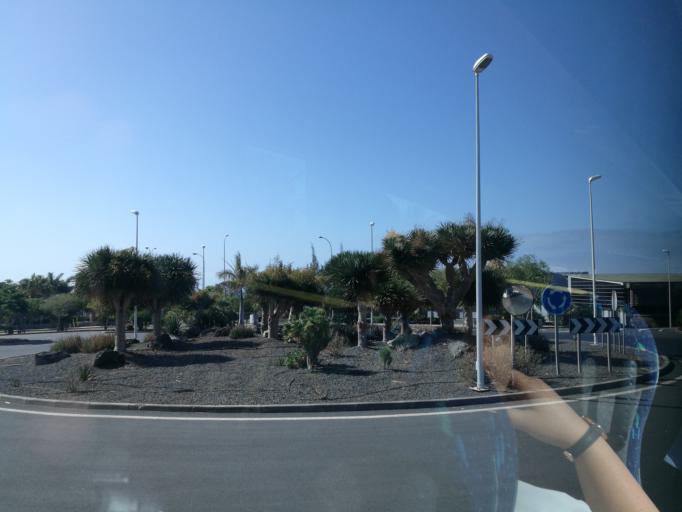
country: ES
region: Canary Islands
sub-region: Provincia de Santa Cruz de Tenerife
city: San Isidro
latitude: 28.0481
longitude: -16.5810
